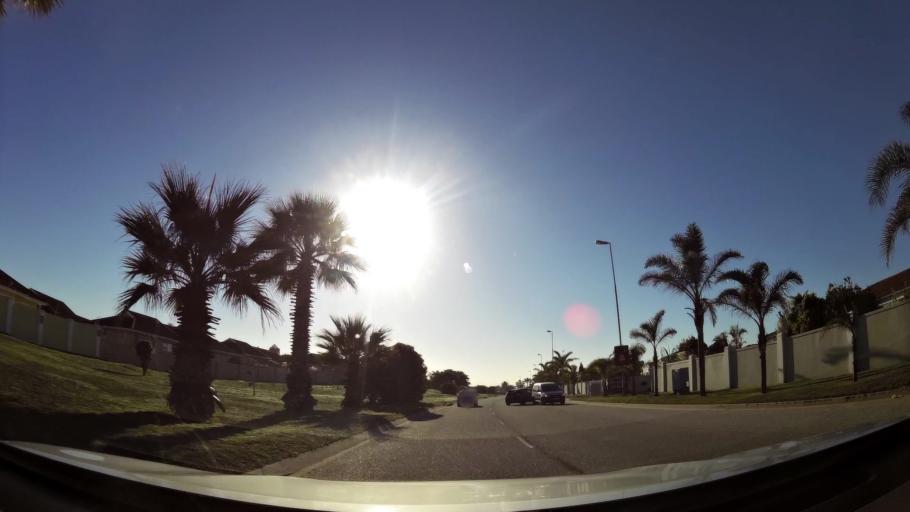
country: ZA
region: Eastern Cape
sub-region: Nelson Mandela Bay Metropolitan Municipality
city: Port Elizabeth
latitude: -33.9908
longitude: 25.6495
